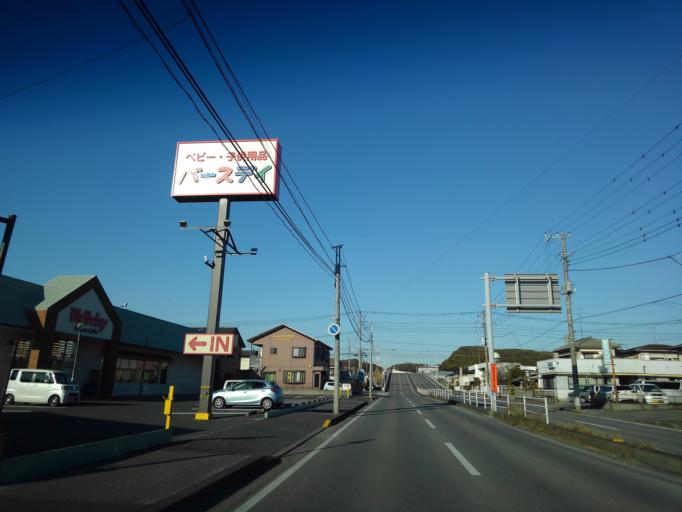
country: JP
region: Chiba
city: Kimitsu
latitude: 35.3330
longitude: 139.8889
